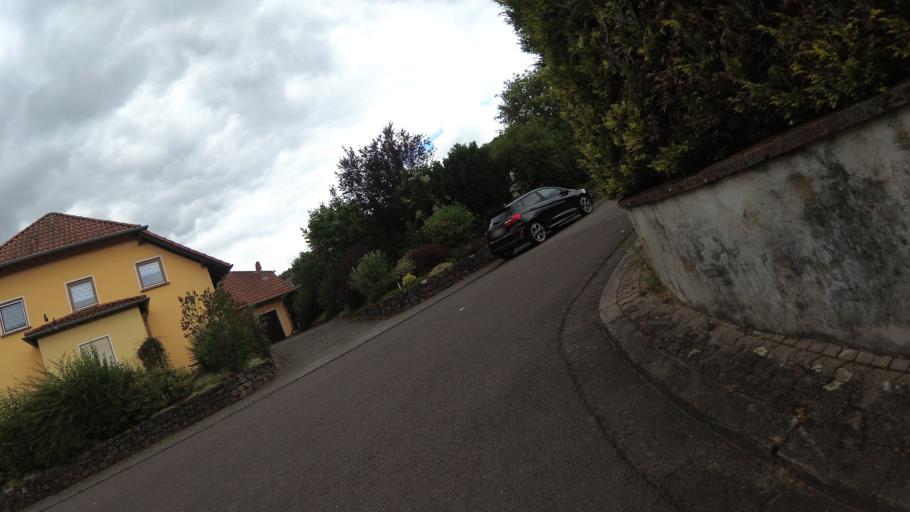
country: DE
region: Saarland
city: Schmelz
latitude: 49.3959
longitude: 6.8350
